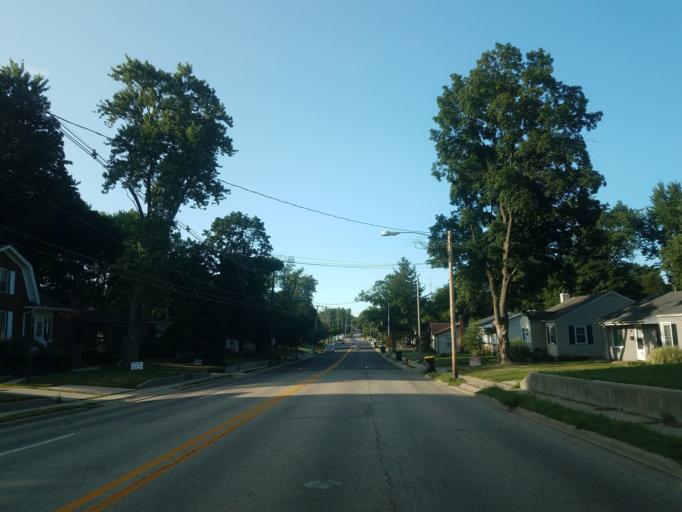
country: US
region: Illinois
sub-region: McLean County
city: Bloomington
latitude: 40.4960
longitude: -88.9820
